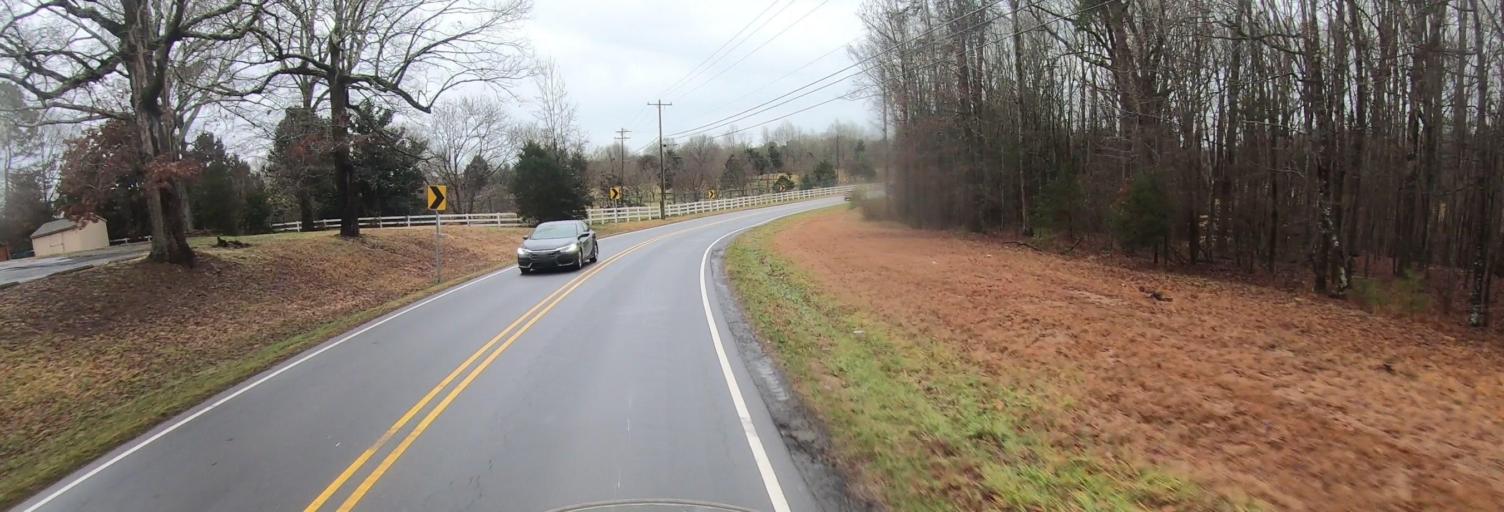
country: US
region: South Carolina
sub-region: York County
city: Lake Wylie
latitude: 35.0832
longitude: -81.0044
